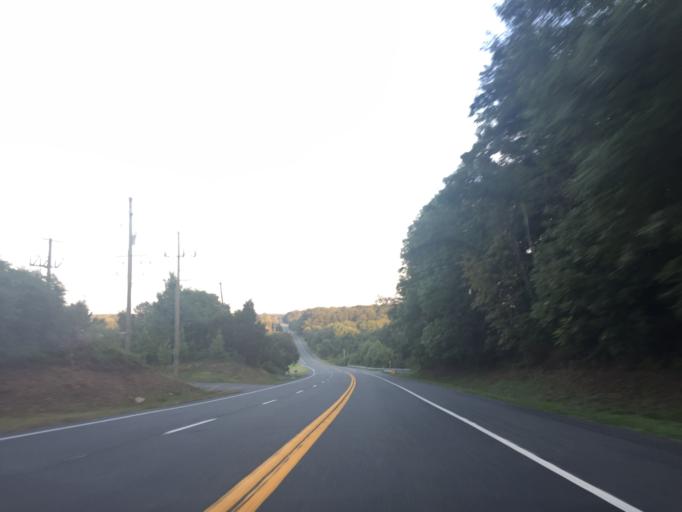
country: US
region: Pennsylvania
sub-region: York County
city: Susquehanna Trails
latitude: 39.7024
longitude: -76.3350
